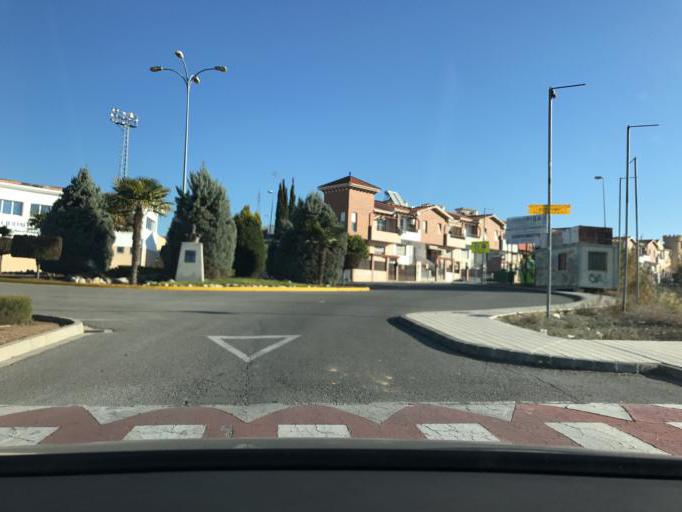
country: ES
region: Andalusia
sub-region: Provincia de Granada
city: Peligros
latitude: 37.2344
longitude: -3.6214
